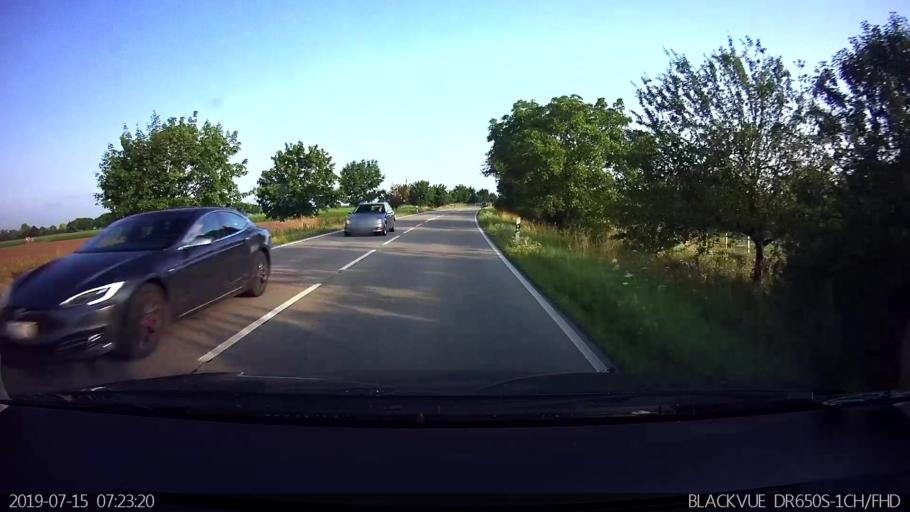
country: DE
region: Baden-Wuerttemberg
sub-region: Freiburg Region
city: Unterkrozingen
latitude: 47.9415
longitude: 7.6800
